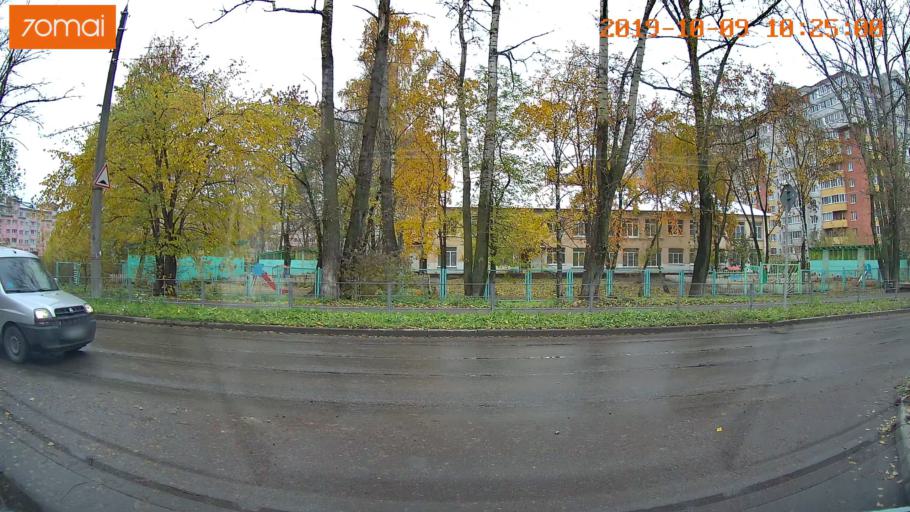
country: RU
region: Vologda
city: Vologda
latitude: 59.2133
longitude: 39.9258
